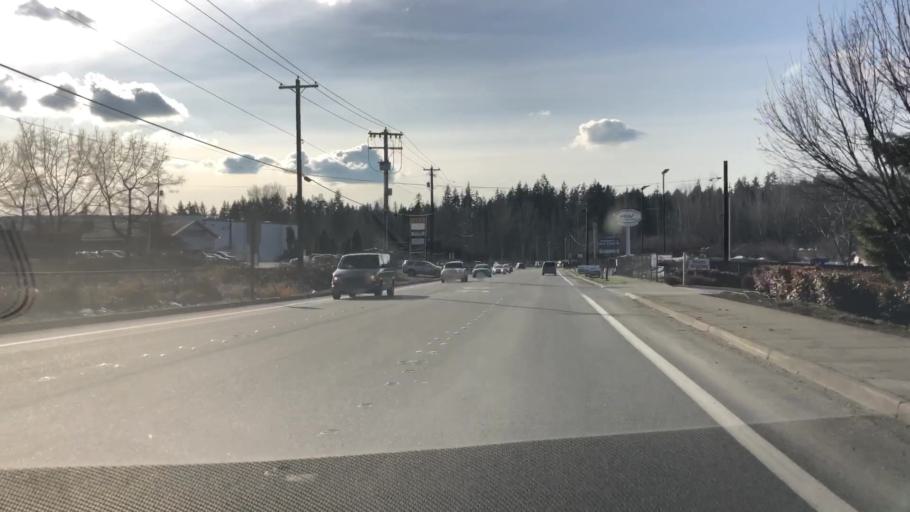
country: US
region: Washington
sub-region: King County
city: Woodinville
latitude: 47.7762
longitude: -122.1472
